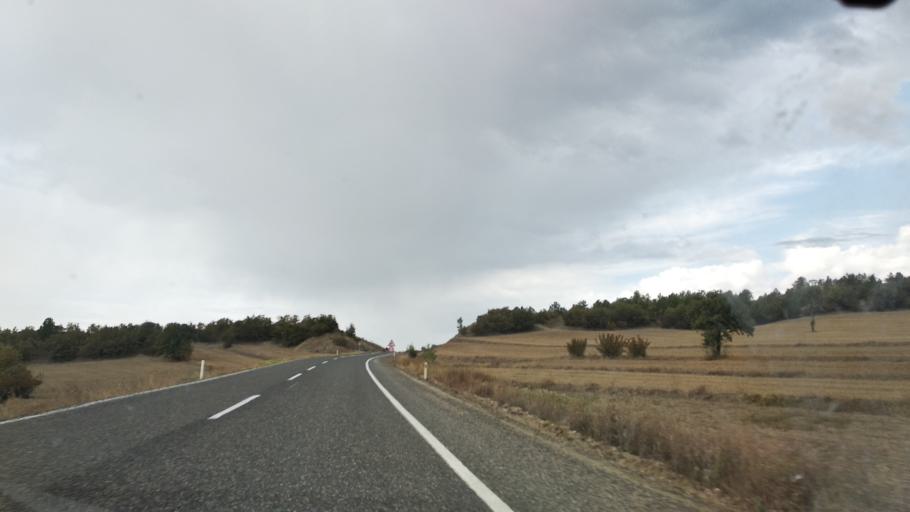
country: TR
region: Bolu
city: Seben
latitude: 40.3328
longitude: 31.4464
